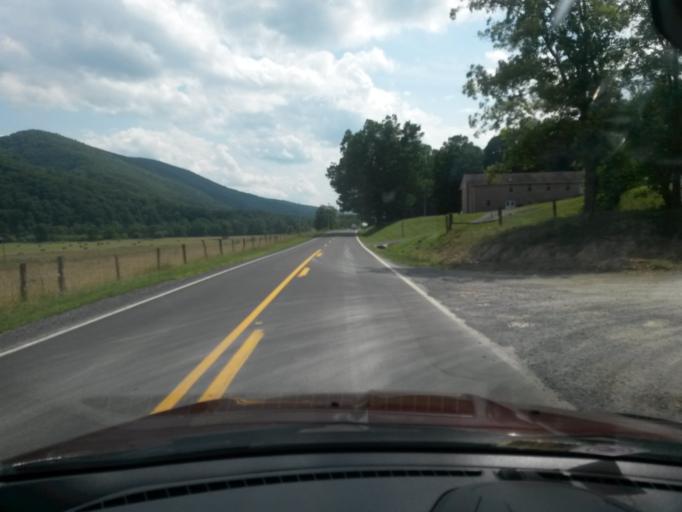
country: US
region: West Virginia
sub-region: Pendleton County
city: Franklin
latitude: 38.5600
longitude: -79.4319
